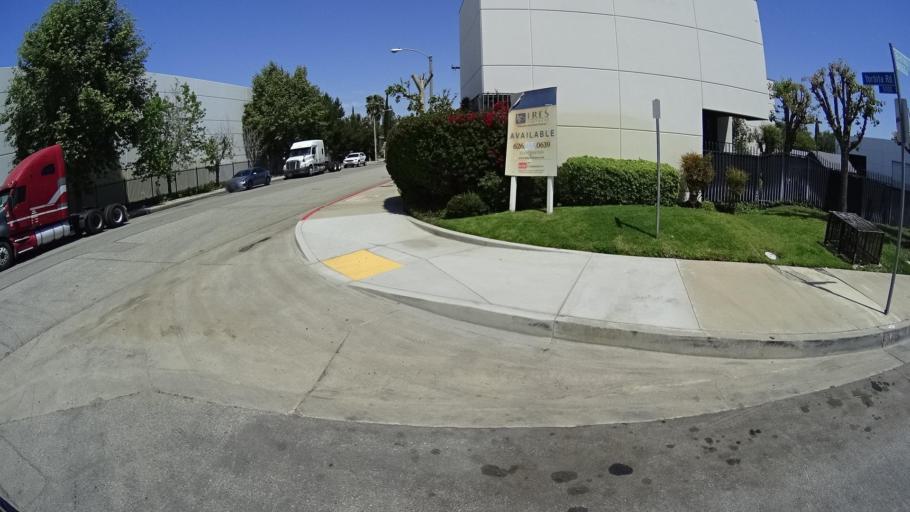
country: US
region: California
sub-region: Los Angeles County
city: South San Jose Hills
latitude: 34.0077
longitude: -117.9034
